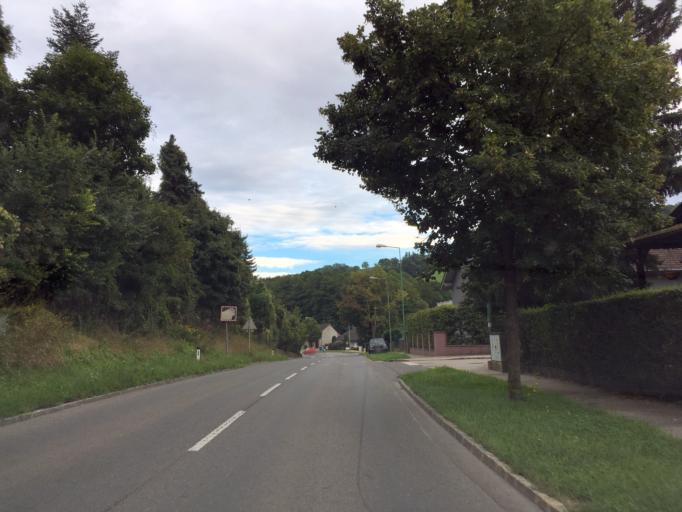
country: AT
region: Lower Austria
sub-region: Politischer Bezirk Tulln
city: Wordern
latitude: 48.3155
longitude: 16.2400
